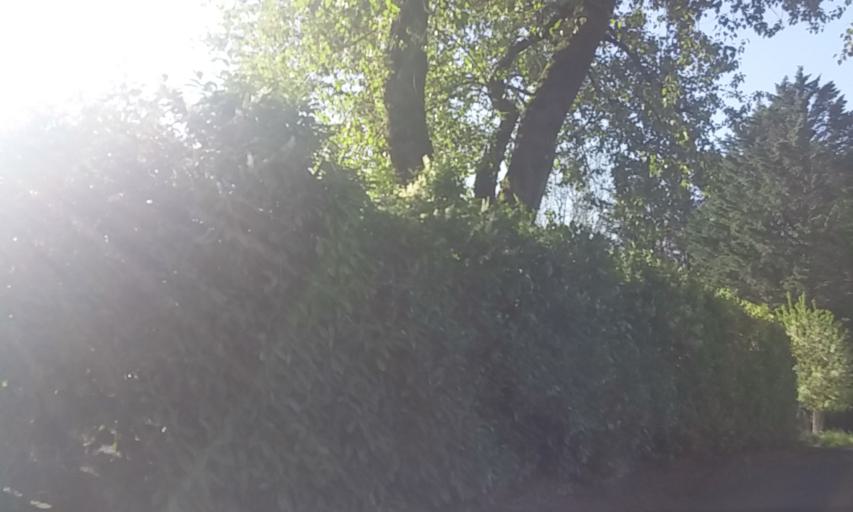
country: US
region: Oregon
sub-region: Washington County
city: Cedar Mill
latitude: 45.5484
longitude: -122.7863
